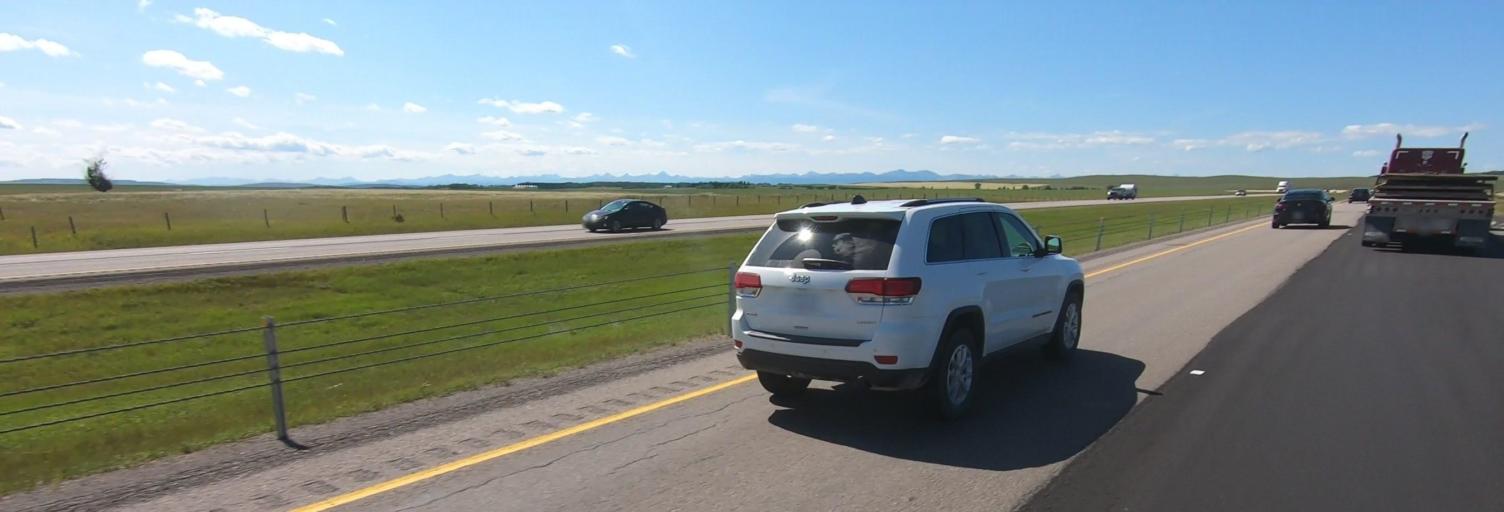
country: CA
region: Alberta
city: Cochrane
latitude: 51.0896
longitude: -114.3984
